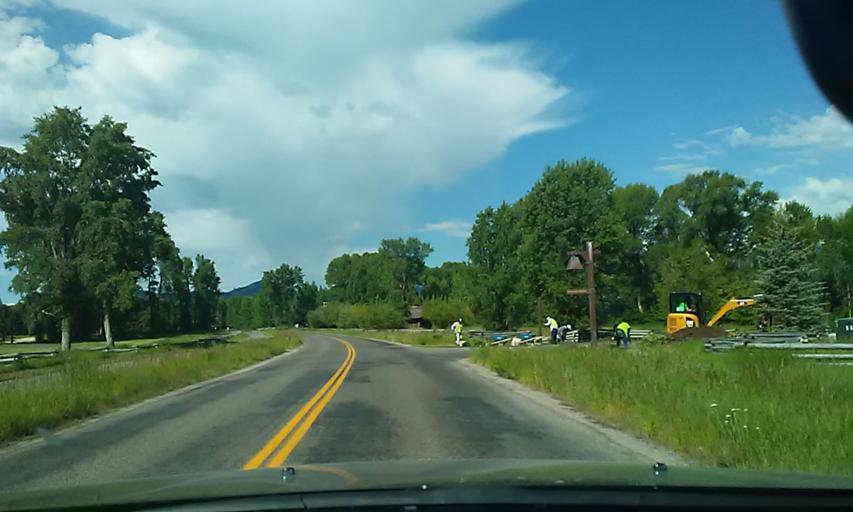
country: US
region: Wyoming
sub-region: Teton County
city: Jackson
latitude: 43.5671
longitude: -110.7455
